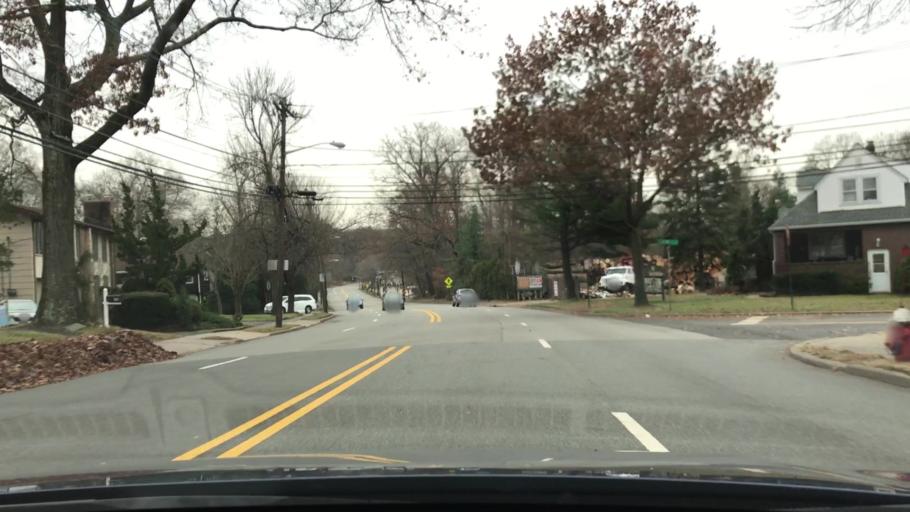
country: US
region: New Jersey
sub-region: Bergen County
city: Paramus
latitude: 40.9538
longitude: -74.0584
